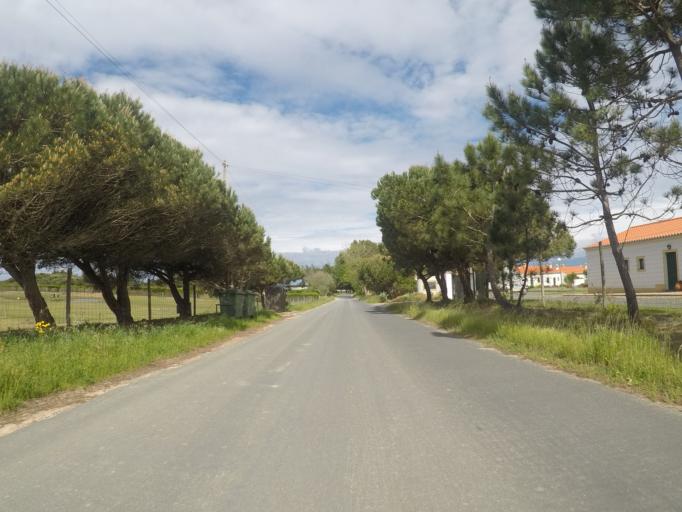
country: PT
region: Beja
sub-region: Odemira
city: Sao Teotonio
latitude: 37.4949
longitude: -8.7863
